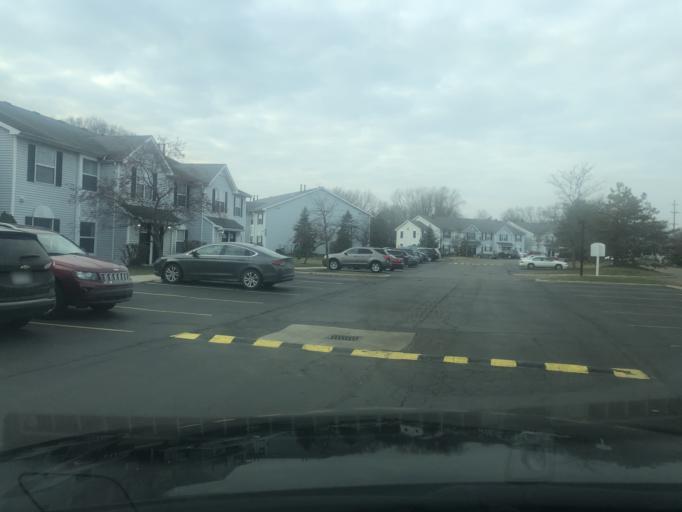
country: US
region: Michigan
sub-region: Wayne County
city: Belleville
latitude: 42.2159
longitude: -83.4922
